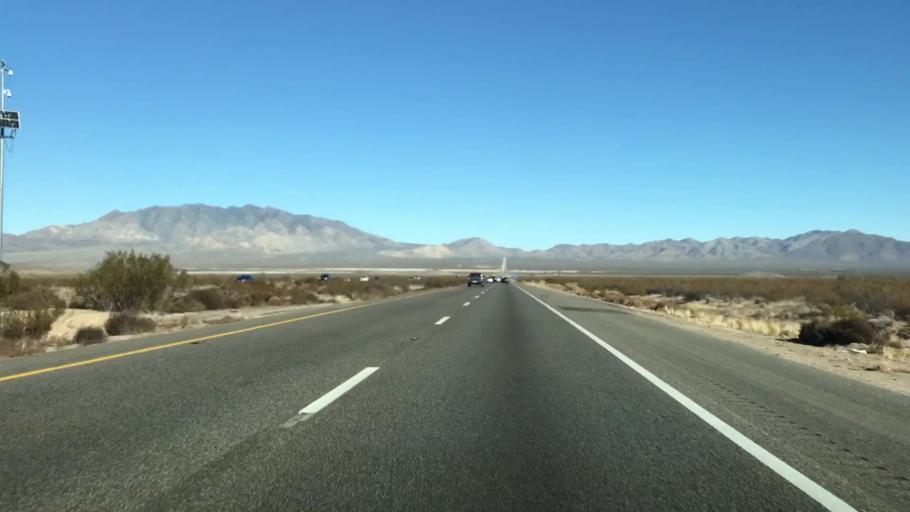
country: US
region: Nevada
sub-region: Clark County
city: Sandy Valley
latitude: 35.4195
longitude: -115.7433
